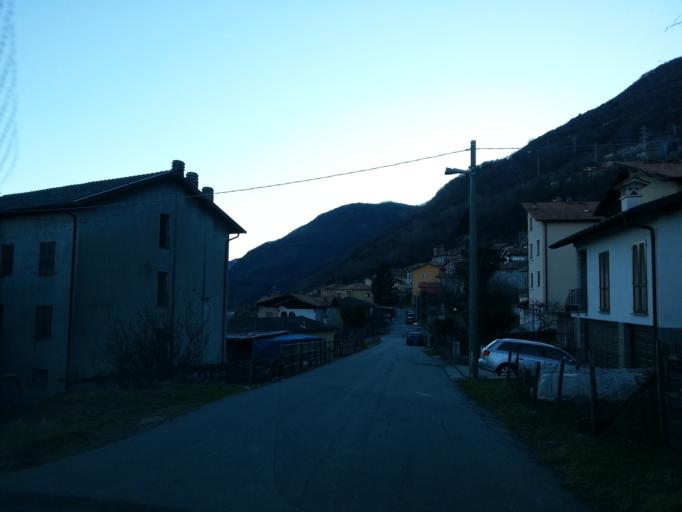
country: IT
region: Lombardy
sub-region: Provincia di Como
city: San Siro
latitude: 46.0701
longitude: 9.2690
